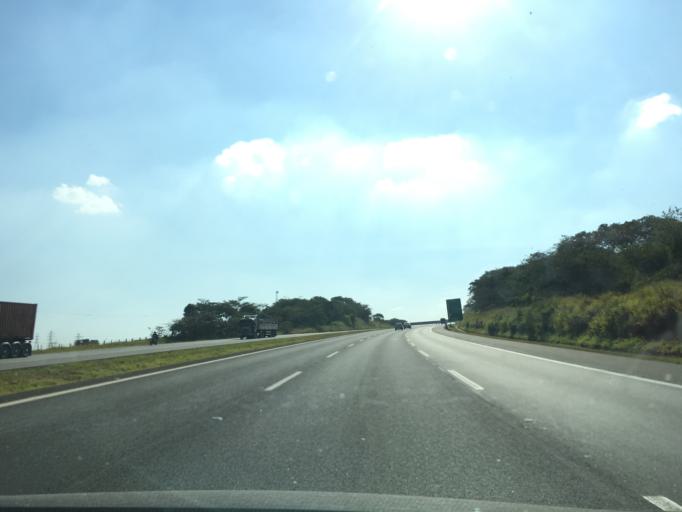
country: BR
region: Sao Paulo
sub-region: Sumare
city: Sumare
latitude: -22.8697
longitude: -47.2765
